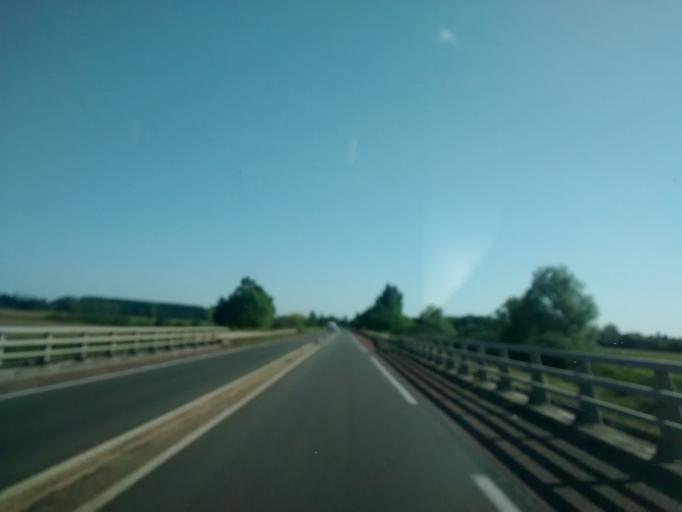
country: FR
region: Aquitaine
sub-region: Departement de la Gironde
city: Libourne
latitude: 44.8819
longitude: -0.2242
